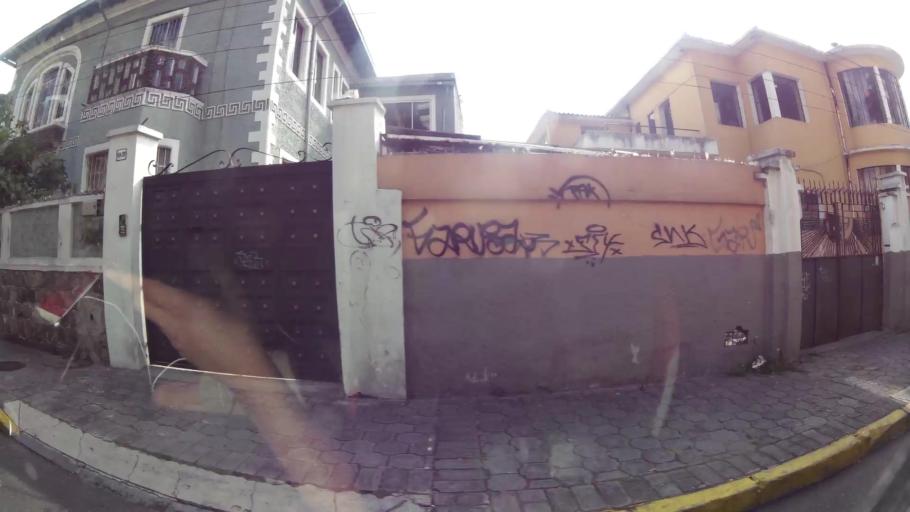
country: EC
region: Pichincha
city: Quito
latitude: -0.2203
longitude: -78.5045
